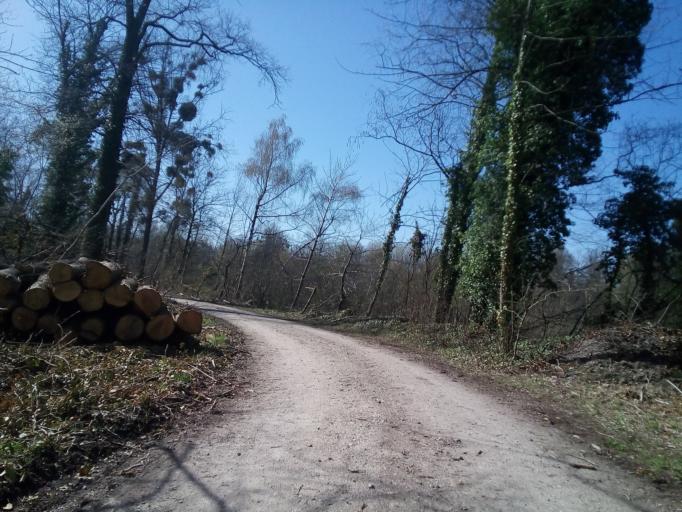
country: DE
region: Baden-Wuerttemberg
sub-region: Freiburg Region
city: Rheinau
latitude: 48.6634
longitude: 7.9060
